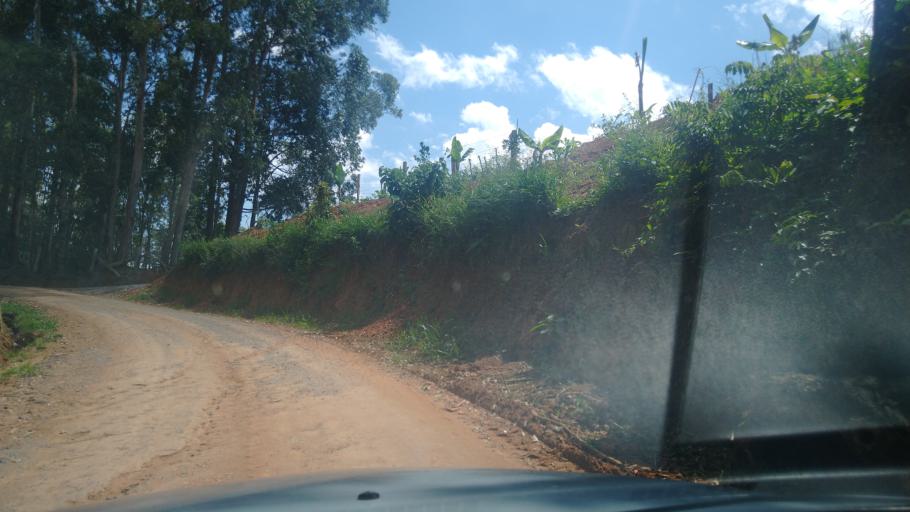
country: BR
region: Minas Gerais
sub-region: Extrema
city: Extrema
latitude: -22.7375
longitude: -46.2950
